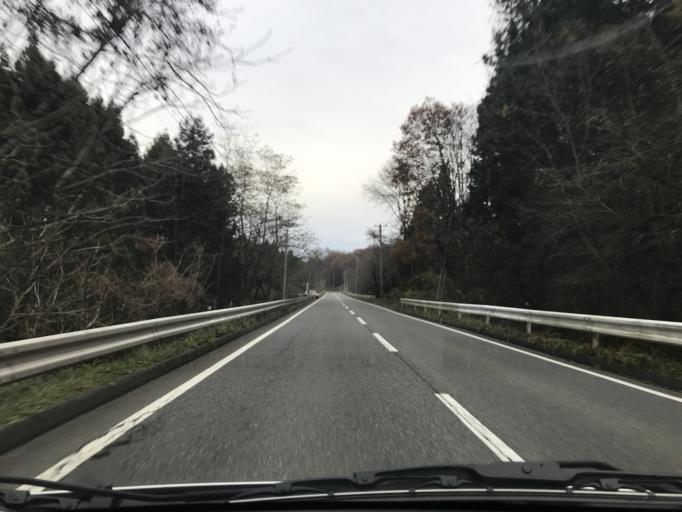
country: JP
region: Iwate
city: Kitakami
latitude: 39.2853
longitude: 141.2278
